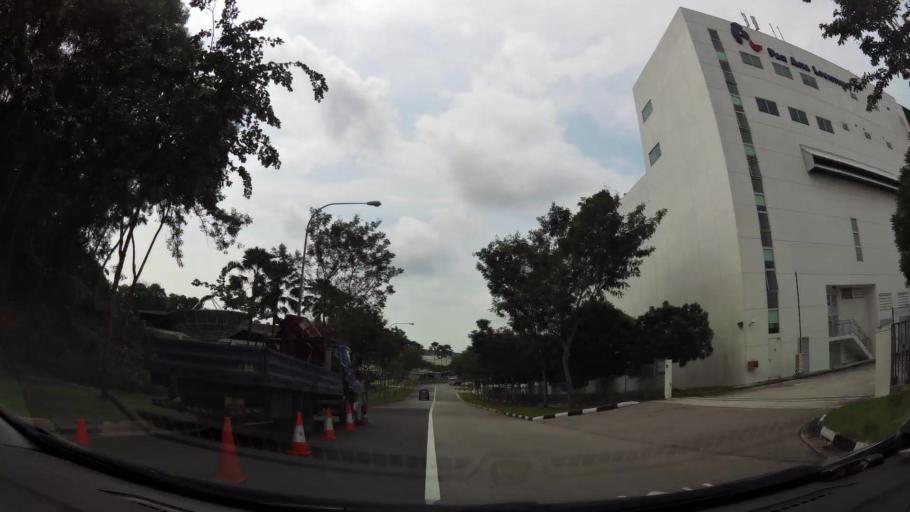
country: SG
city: Singapore
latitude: 1.3538
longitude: 103.9747
